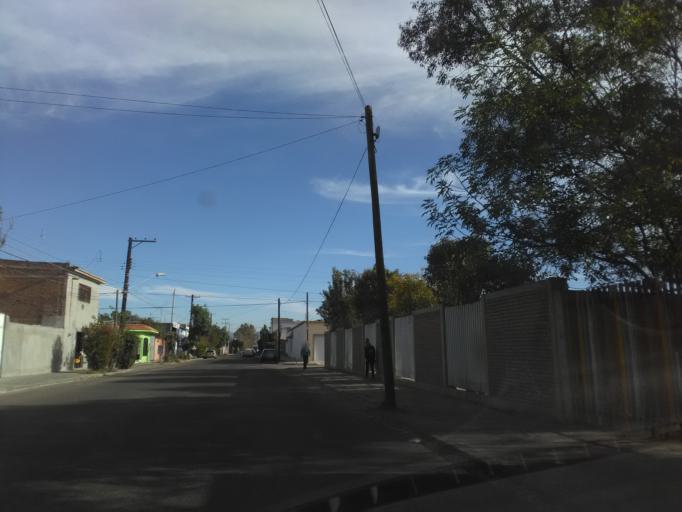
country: MX
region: Durango
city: Victoria de Durango
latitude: 24.0308
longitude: -104.6317
